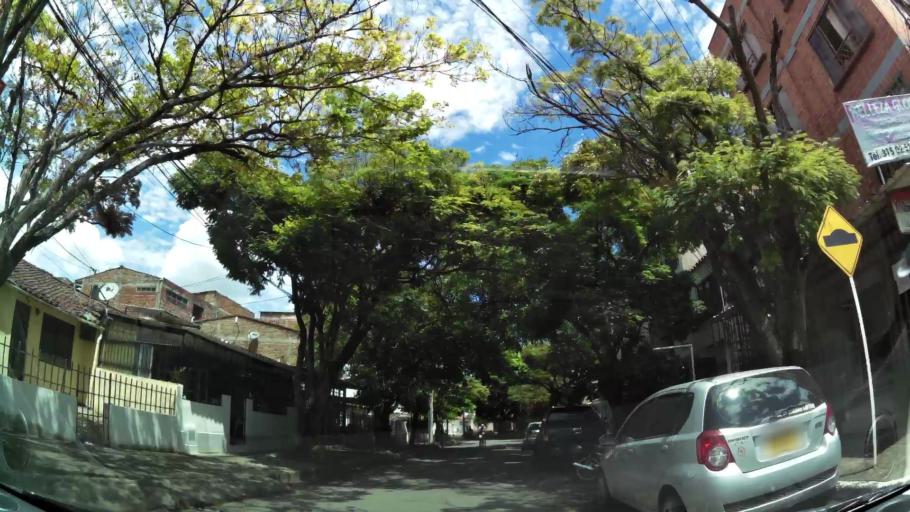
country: CO
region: Valle del Cauca
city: Cali
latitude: 3.3854
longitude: -76.5226
